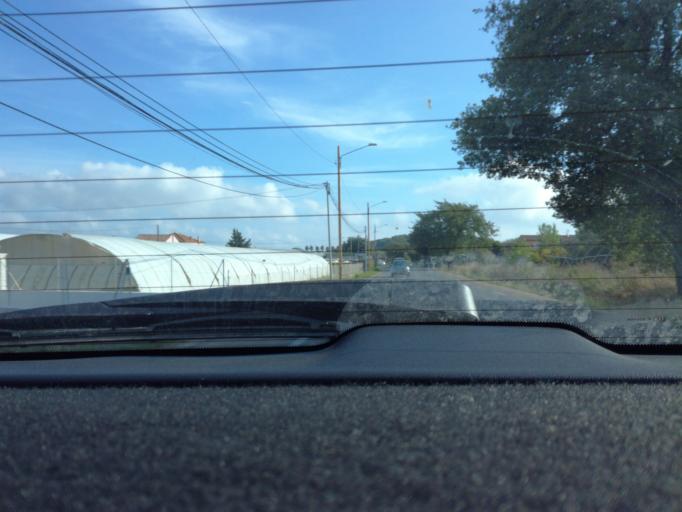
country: FR
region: Provence-Alpes-Cote d'Azur
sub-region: Departement du Var
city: Hyeres
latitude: 43.0903
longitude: 6.1292
